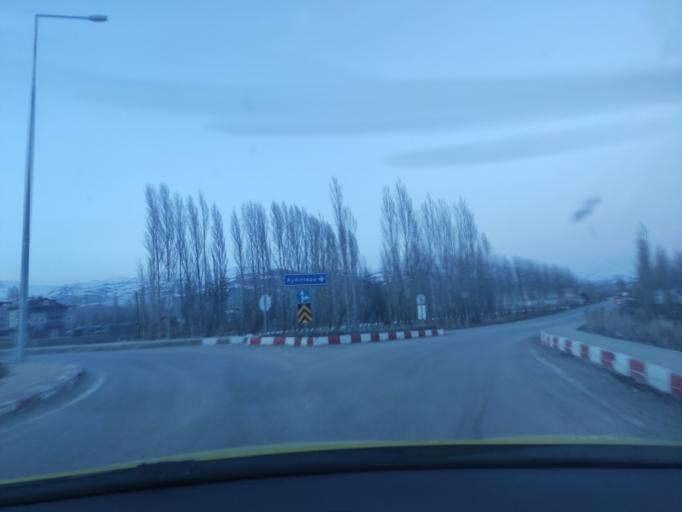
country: TR
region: Bayburt
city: Aydintepe
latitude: 40.3599
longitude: 40.1011
